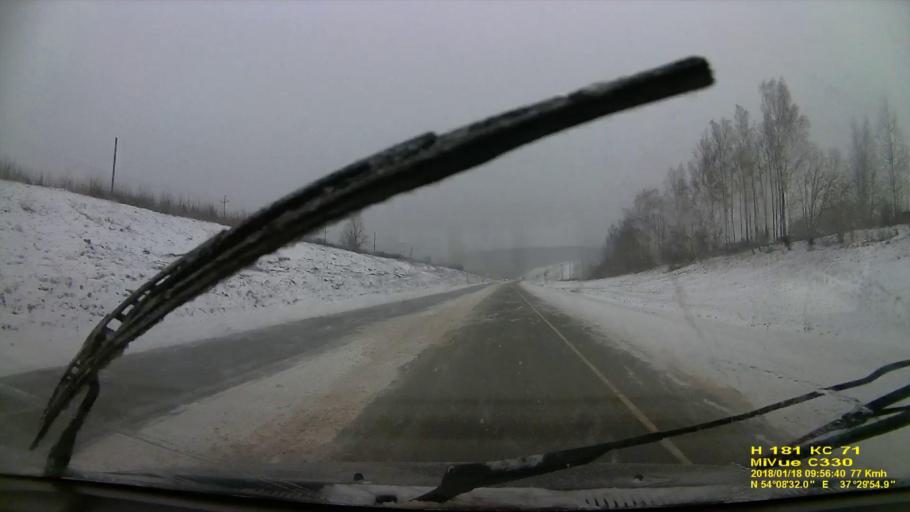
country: RU
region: Tula
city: Kosaya Gora
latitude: 54.1421
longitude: 37.4986
